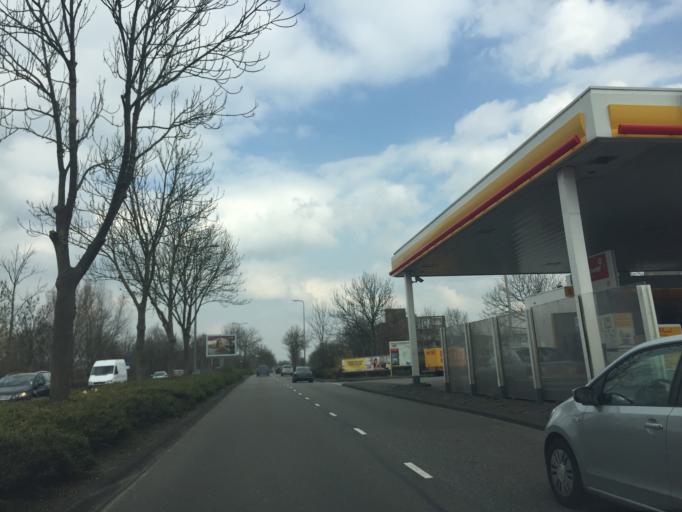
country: NL
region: South Holland
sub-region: Gemeente Alphen aan den Rijn
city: Alphen aan den Rijn
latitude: 52.1494
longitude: 4.6589
